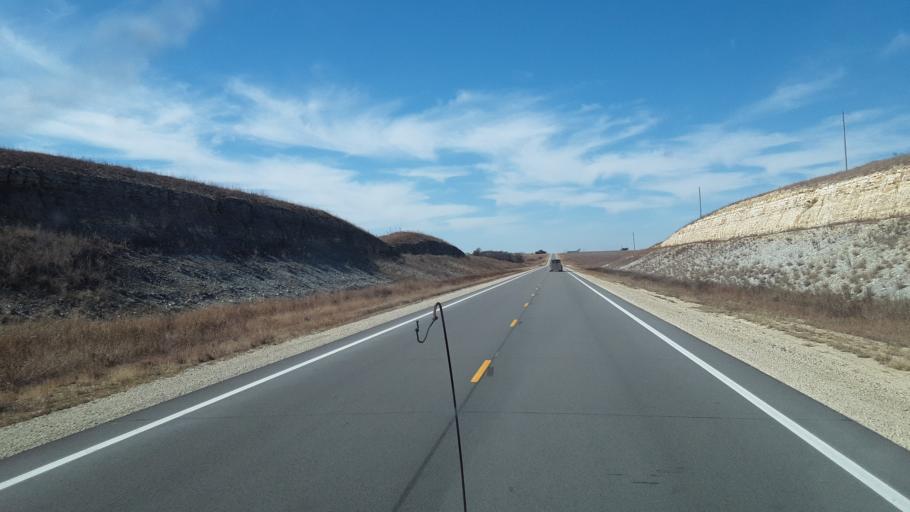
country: US
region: Kansas
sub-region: Chase County
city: Cottonwood Falls
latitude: 38.3628
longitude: -96.7779
